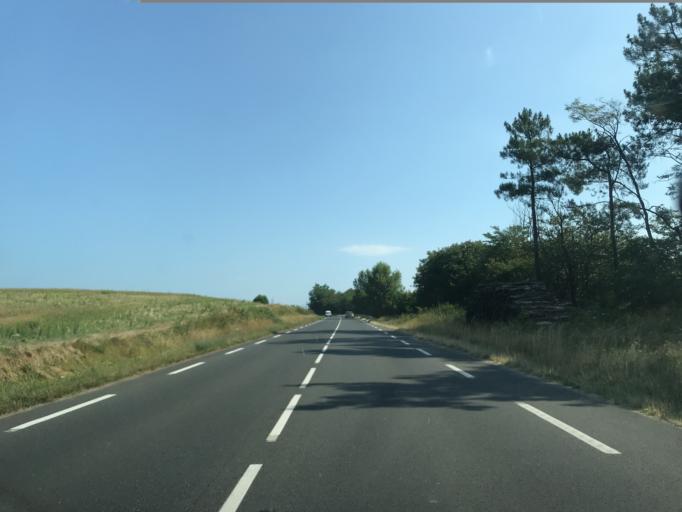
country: FR
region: Aquitaine
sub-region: Departement de la Dordogne
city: Sarlat-la-Caneda
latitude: 44.9467
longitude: 1.2222
